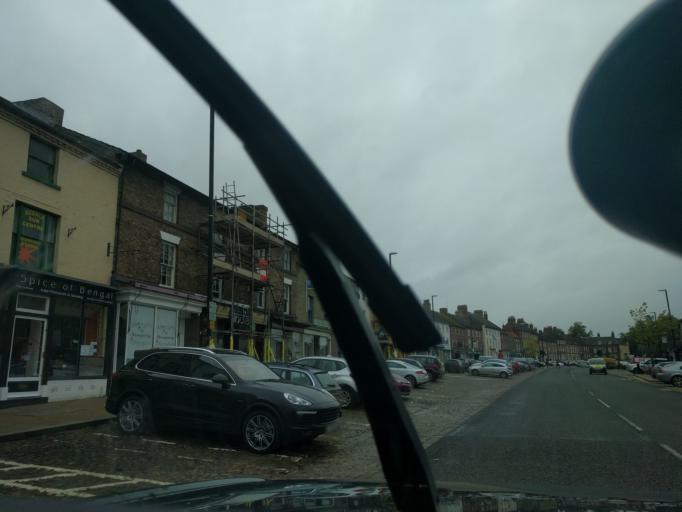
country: GB
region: England
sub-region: North Yorkshire
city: Bedale
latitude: 54.2883
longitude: -1.5918
